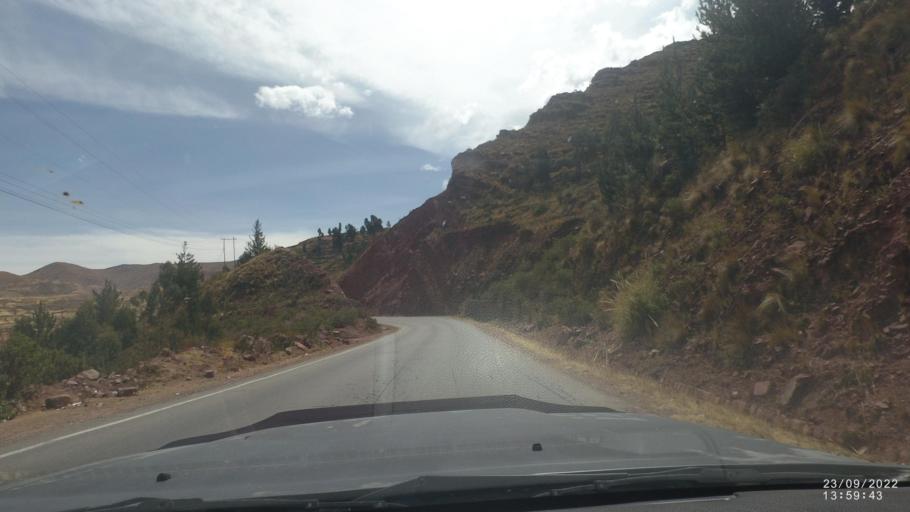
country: BO
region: Cochabamba
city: Irpa Irpa
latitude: -17.7192
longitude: -66.5671
